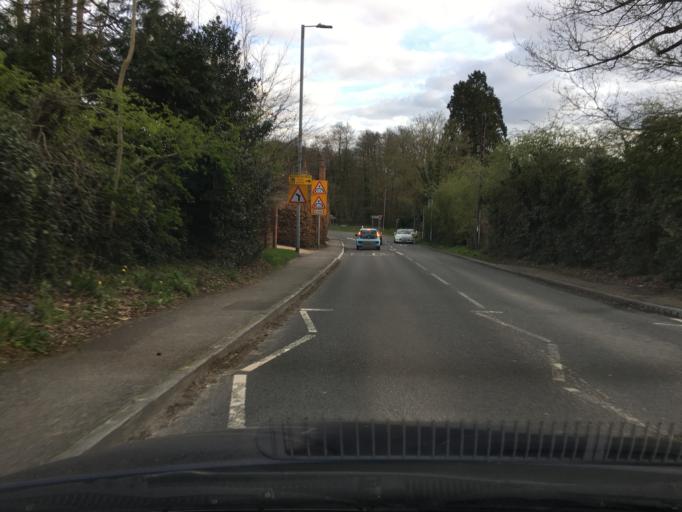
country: GB
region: England
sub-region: Hampshire
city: Yateley
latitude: 51.3493
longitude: -0.8137
